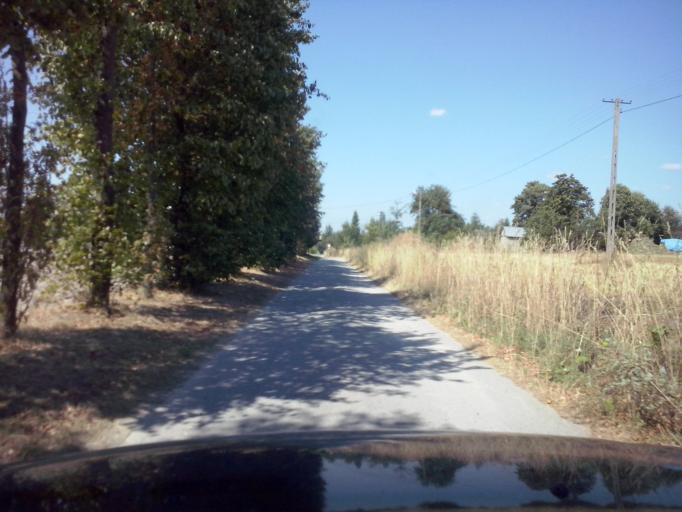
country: PL
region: Swietokrzyskie
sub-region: Powiat buski
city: Gnojno
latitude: 50.5972
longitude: 20.8986
